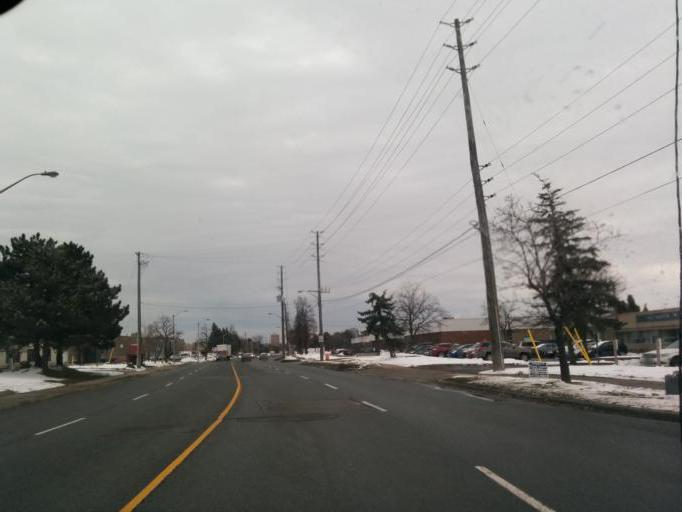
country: CA
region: Ontario
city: Etobicoke
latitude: 43.7459
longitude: -79.6220
